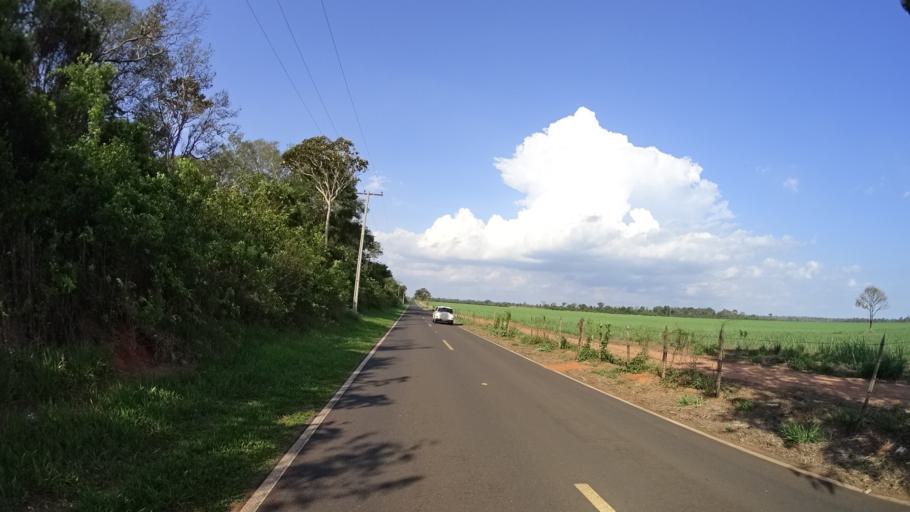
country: BR
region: Sao Paulo
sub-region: Urupes
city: Urupes
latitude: -21.3866
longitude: -49.4973
